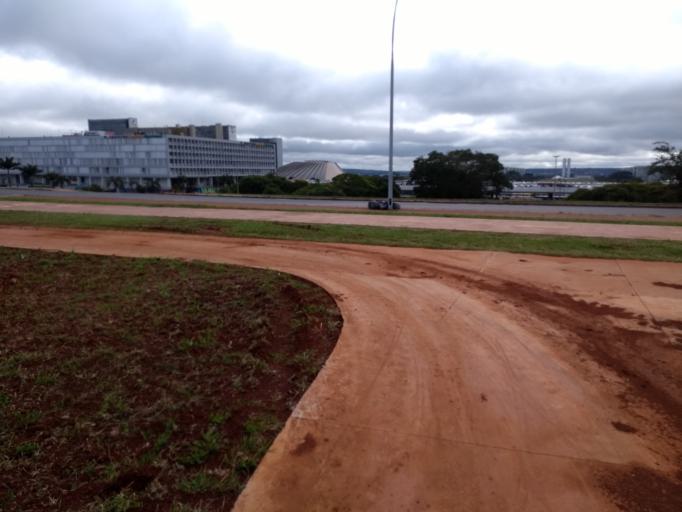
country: BR
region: Federal District
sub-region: Brasilia
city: Brasilia
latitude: -15.7931
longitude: -47.8860
